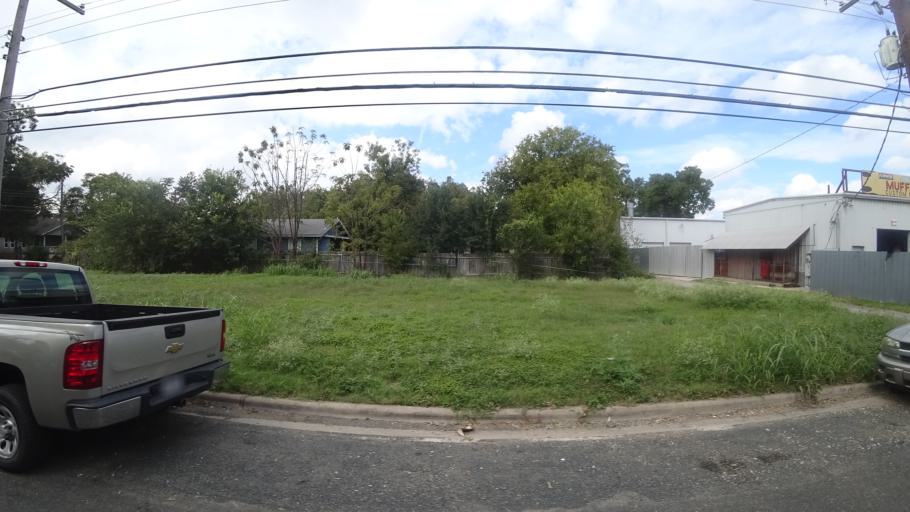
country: US
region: Texas
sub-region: Travis County
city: Austin
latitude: 30.2557
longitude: -97.7104
